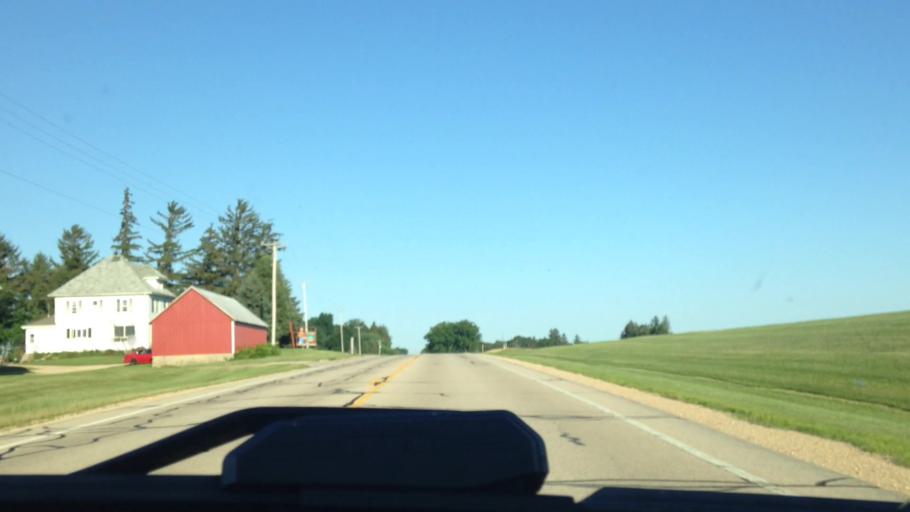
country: US
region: Wisconsin
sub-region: Dane County
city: De Forest
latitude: 43.3324
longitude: -89.2912
